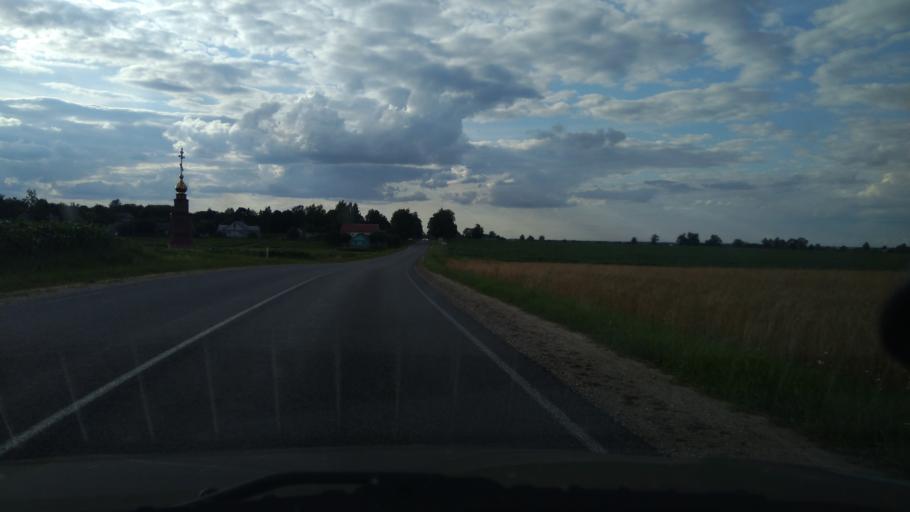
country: BY
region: Grodnenskaya
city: Masty
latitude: 53.3167
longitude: 24.6900
